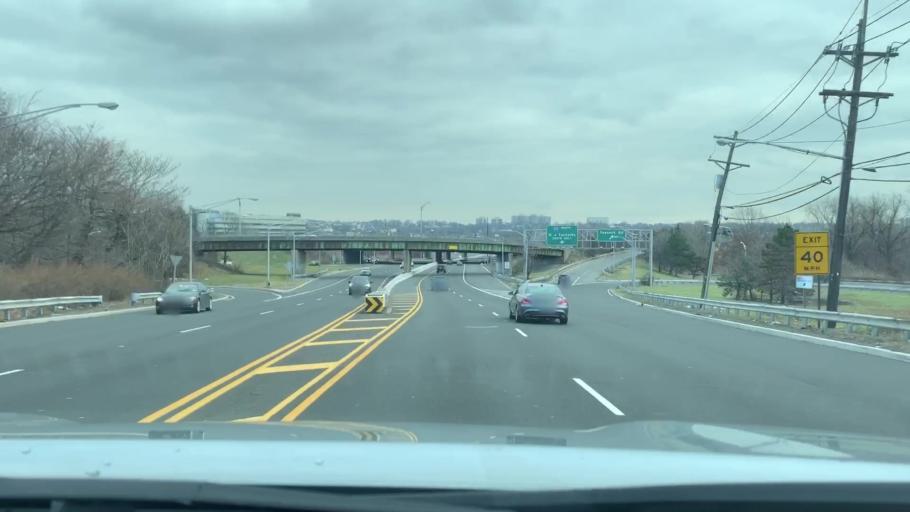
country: US
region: New Jersey
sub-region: Bergen County
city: Ridgefield Park
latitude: 40.8481
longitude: -74.0211
